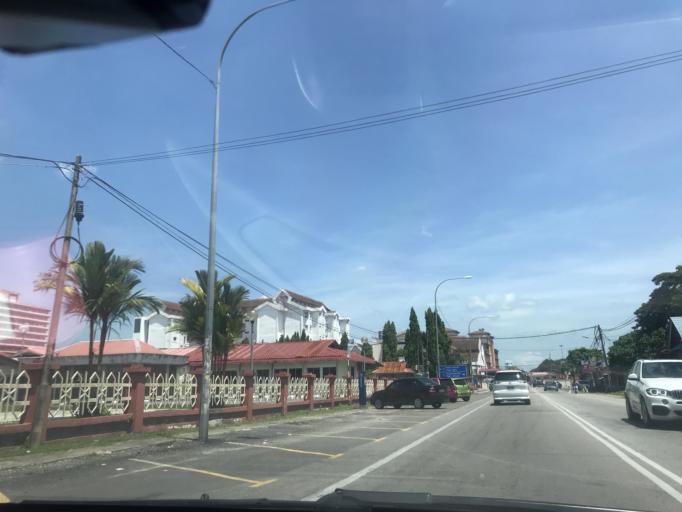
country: MY
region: Kelantan
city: Kota Bharu
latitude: 6.1247
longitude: 102.2485
